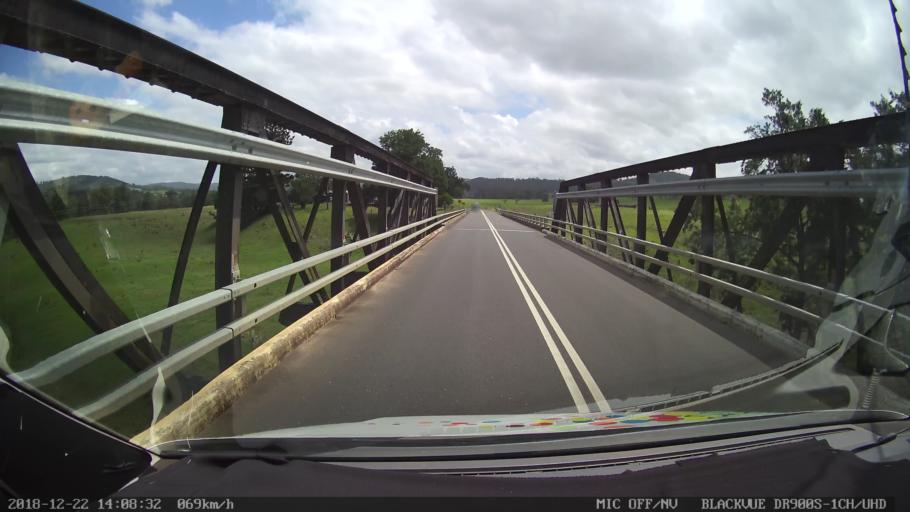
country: AU
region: New South Wales
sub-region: Clarence Valley
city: Coutts Crossing
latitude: -29.9792
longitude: 152.7247
